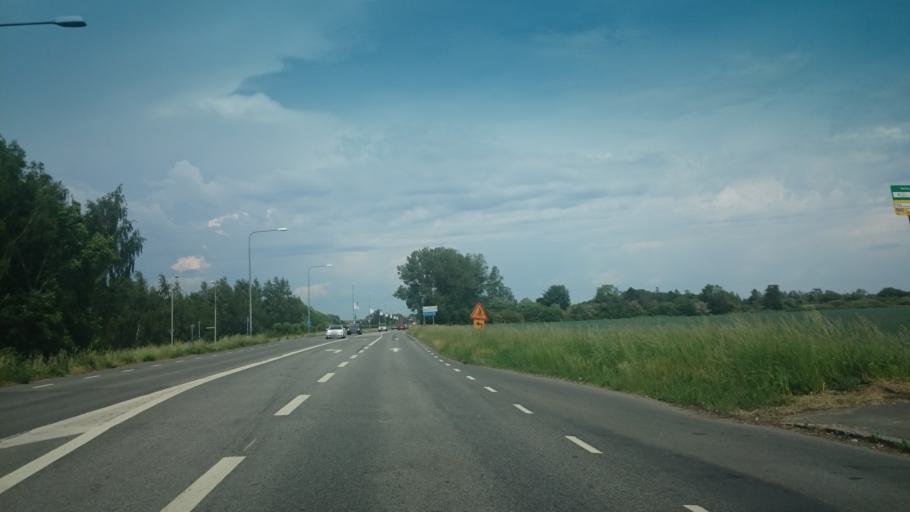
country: SE
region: Skane
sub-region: Kristianstads Kommun
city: Norra Asum
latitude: 56.0026
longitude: 14.1509
